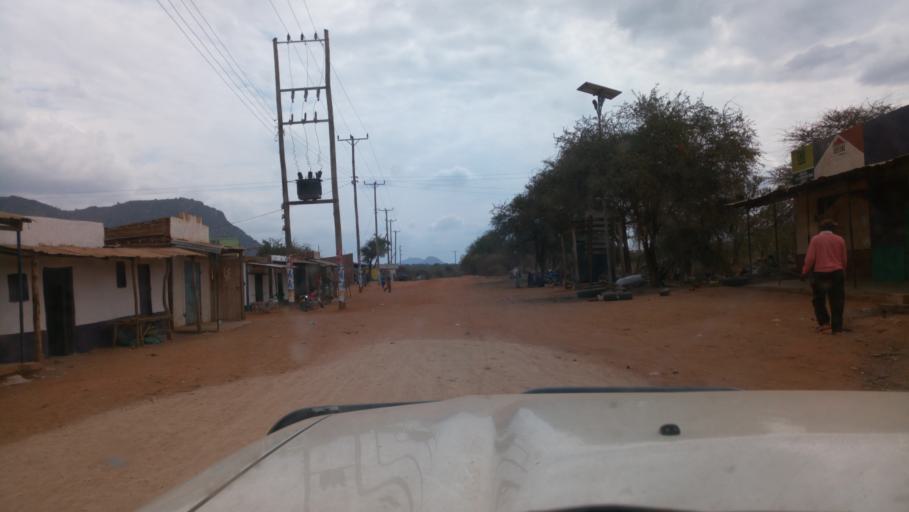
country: KE
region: Kitui
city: Kitui
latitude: -1.8091
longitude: 38.4284
